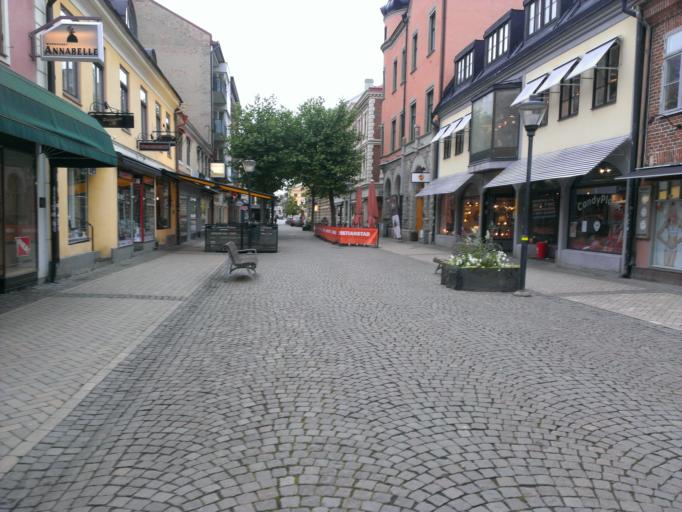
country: SE
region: Skane
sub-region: Kristianstads Kommun
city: Kristianstad
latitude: 56.0299
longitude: 14.1556
